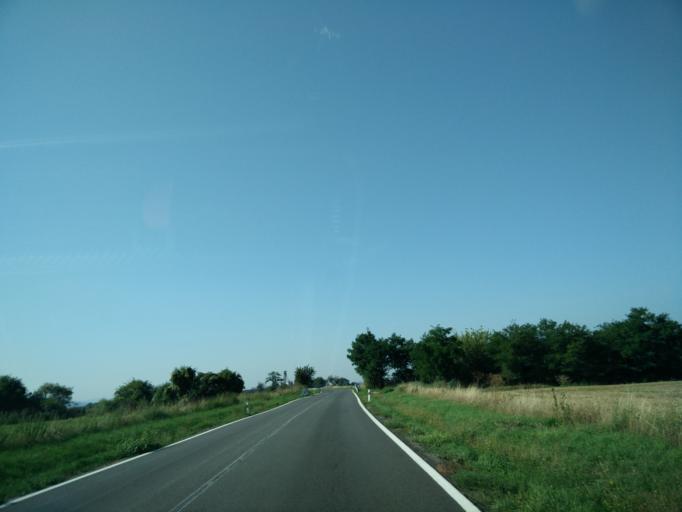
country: SK
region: Nitriansky
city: Banovce nad Bebravou
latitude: 48.5271
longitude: 18.1869
